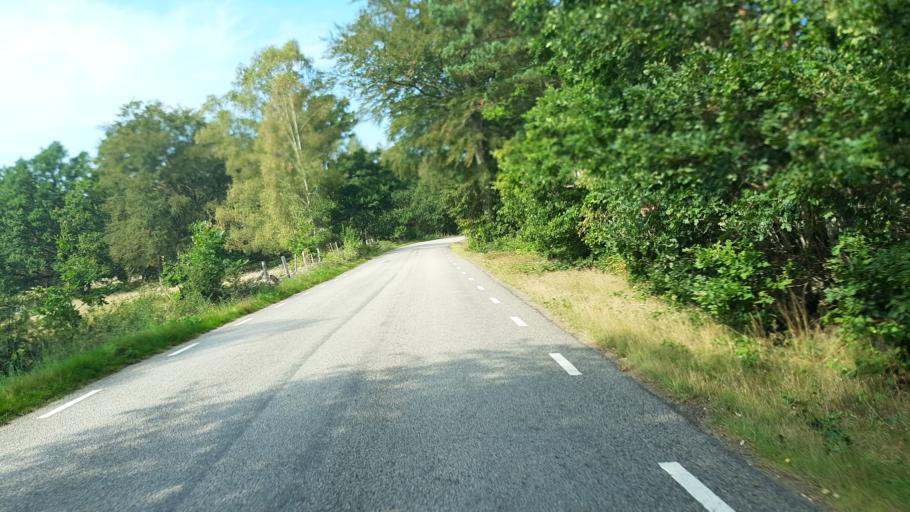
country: SE
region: Blekinge
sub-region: Karlskrona Kommun
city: Nattraby
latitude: 56.2190
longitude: 15.4337
